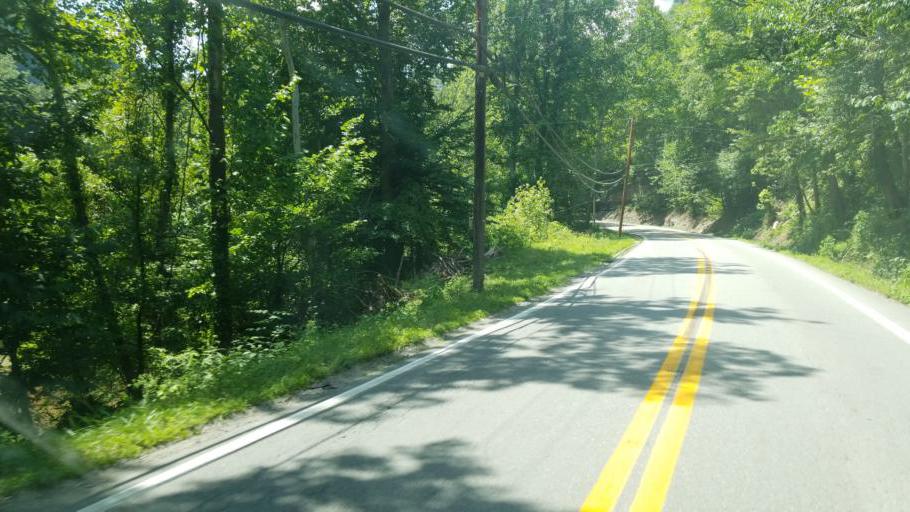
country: US
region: West Virginia
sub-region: Kanawha County
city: Chesapeake
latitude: 38.1731
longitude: -81.4468
